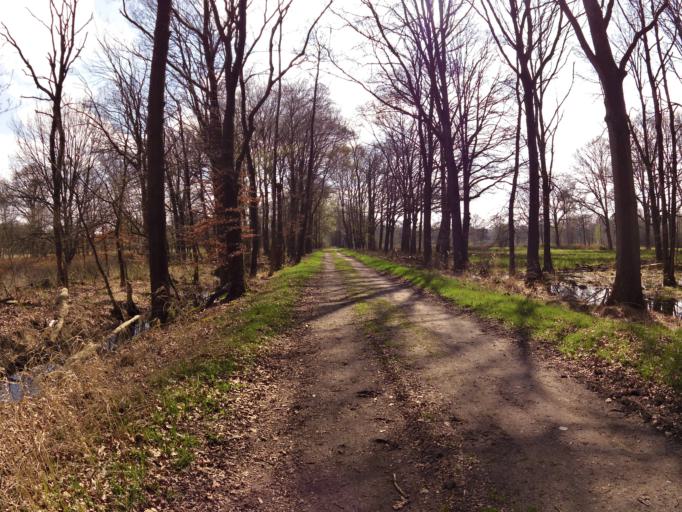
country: NL
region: North Brabant
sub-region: Gemeente Haaren
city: Haaren
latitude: 51.5593
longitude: 5.2631
